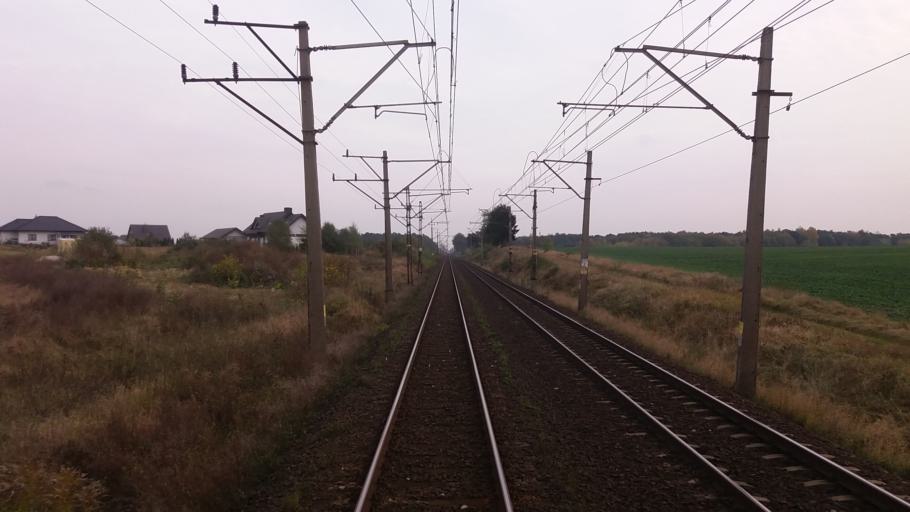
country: PL
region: West Pomeranian Voivodeship
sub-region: Powiat stargardzki
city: Stargard Szczecinski
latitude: 53.3597
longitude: 14.9620
